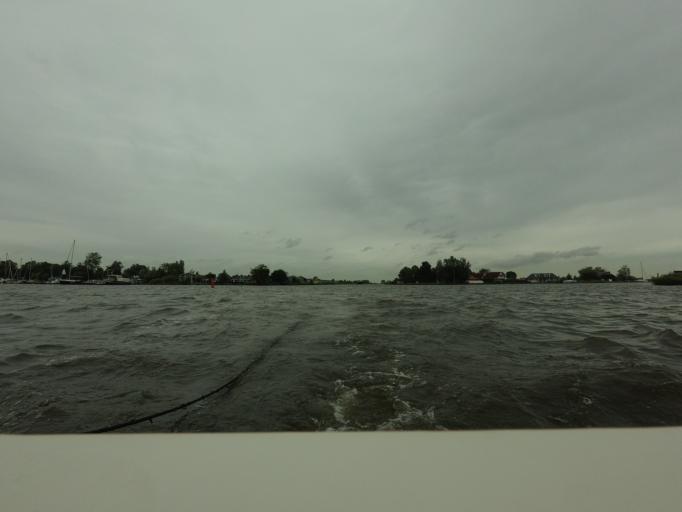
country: NL
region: Friesland
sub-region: Gemeente Boarnsterhim
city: Grou
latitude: 53.0983
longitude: 5.8483
